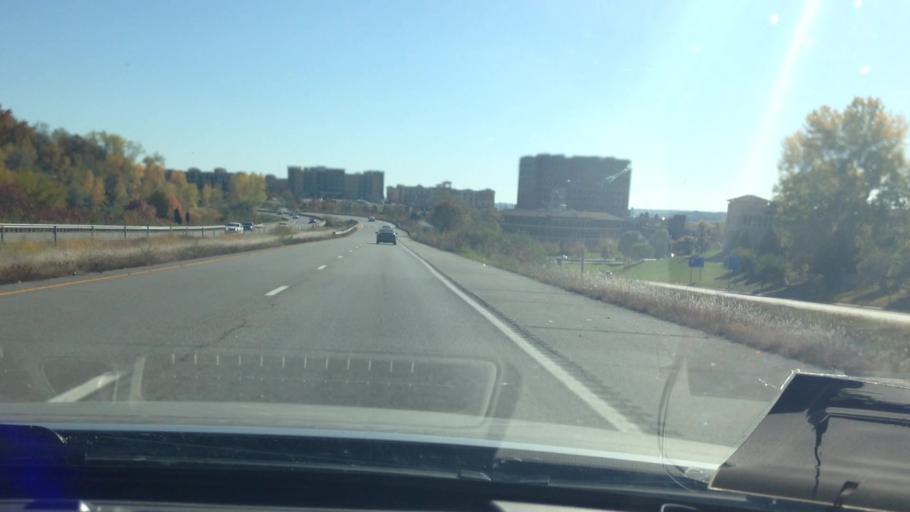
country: US
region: Missouri
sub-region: Platte County
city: Riverside
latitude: 39.1716
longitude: -94.5949
